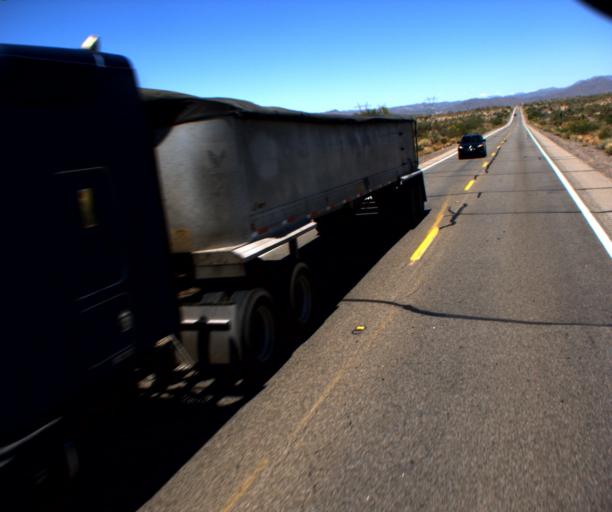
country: US
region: Arizona
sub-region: Yavapai County
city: Bagdad
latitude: 34.3251
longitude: -113.1385
